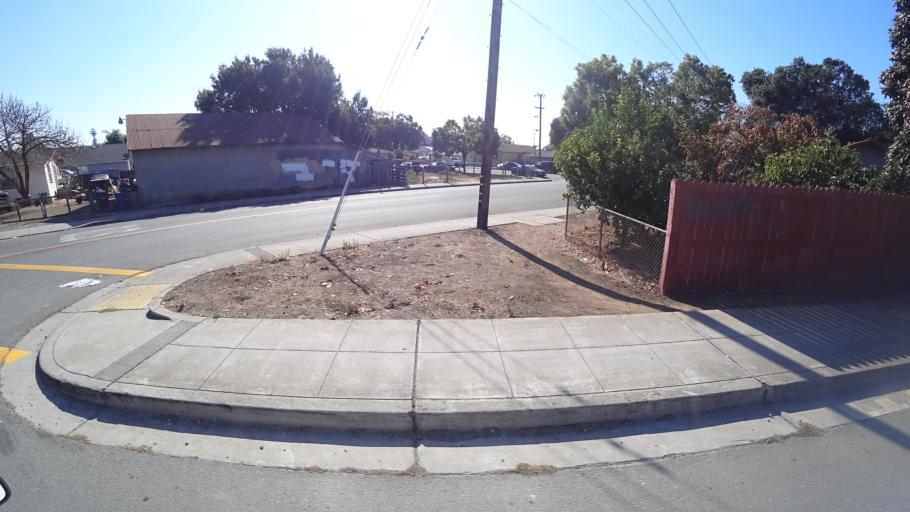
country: US
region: California
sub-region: Alameda County
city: Union City
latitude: 37.6059
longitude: -122.0266
